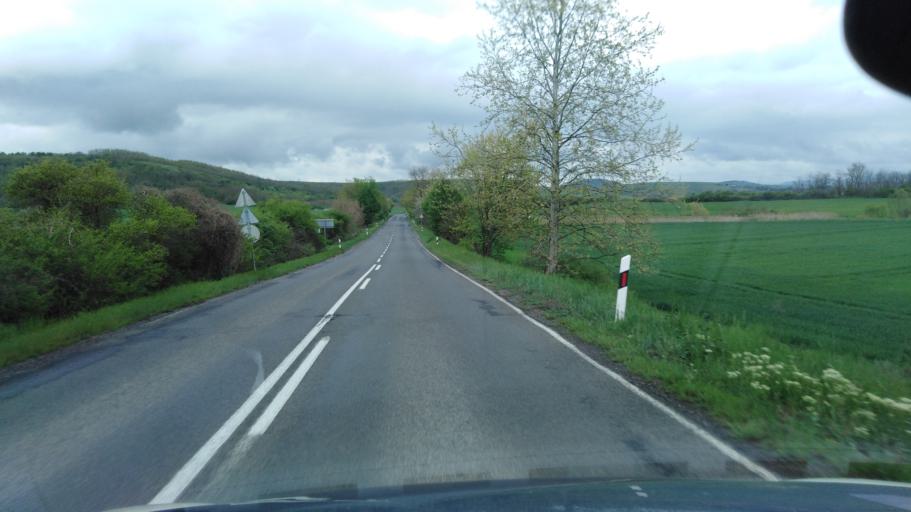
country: HU
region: Nograd
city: Szecseny
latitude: 48.1219
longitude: 19.5517
